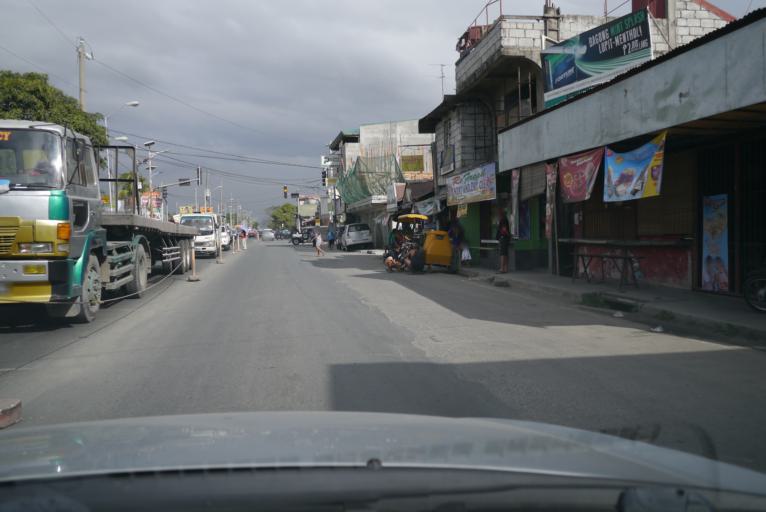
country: PH
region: Calabarzon
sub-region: Province of Rizal
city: Taytay
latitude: 14.5490
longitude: 121.1210
